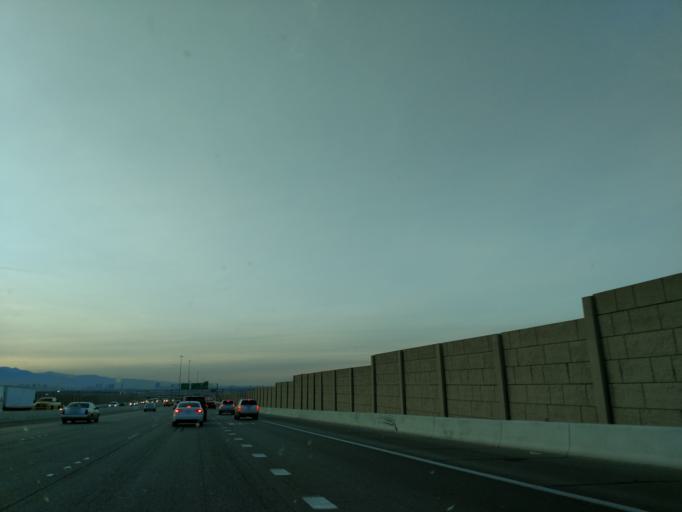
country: US
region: Nevada
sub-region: Clark County
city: Henderson
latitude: 36.0253
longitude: -115.0041
